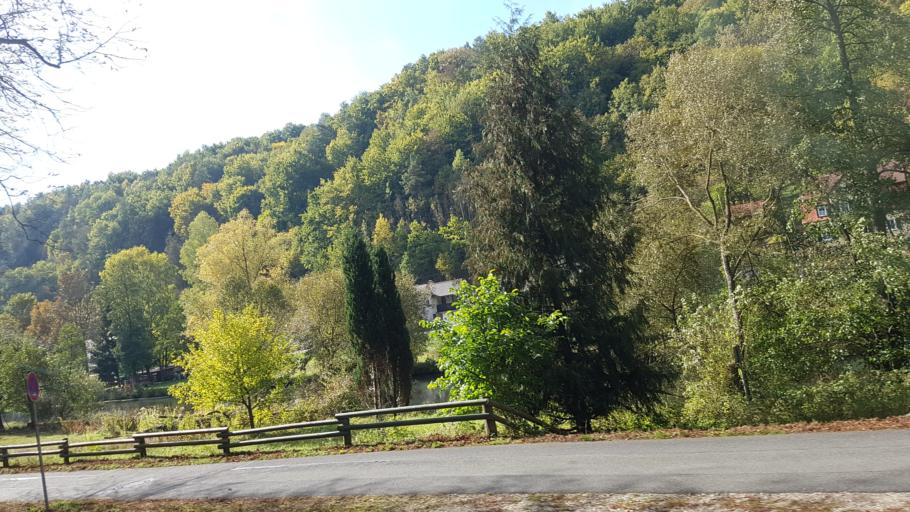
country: DE
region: Bavaria
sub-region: Upper Franconia
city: Waischenfeld
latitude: 49.8404
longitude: 11.3482
